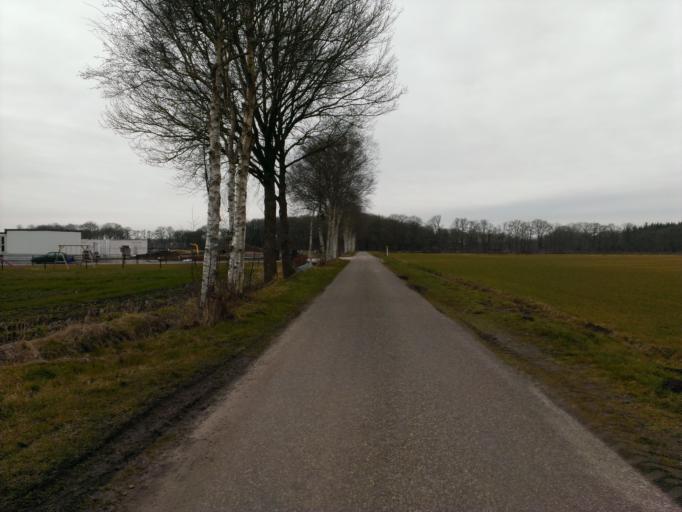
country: NL
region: Drenthe
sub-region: Gemeente Hoogeveen
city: Hoogeveen
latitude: 52.7614
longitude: 6.4651
